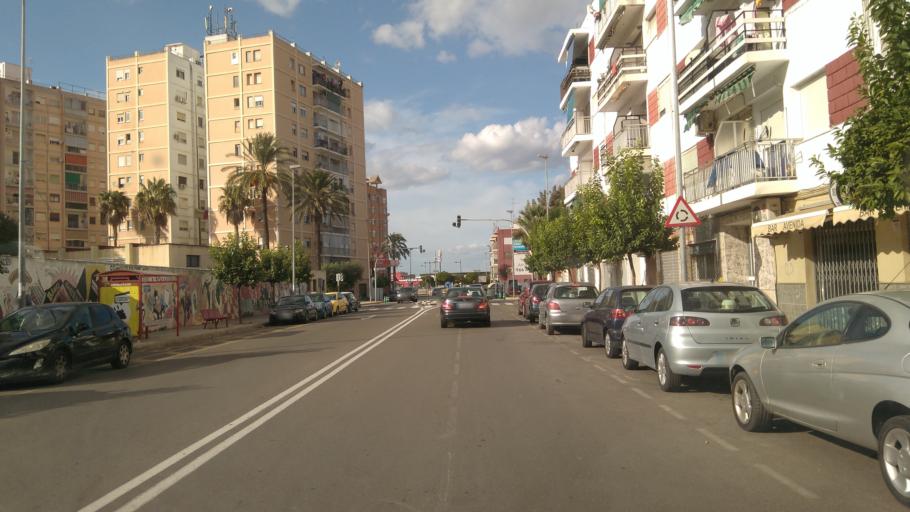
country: ES
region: Valencia
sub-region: Provincia de Valencia
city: Alzira
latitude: 39.1578
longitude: -0.4288
